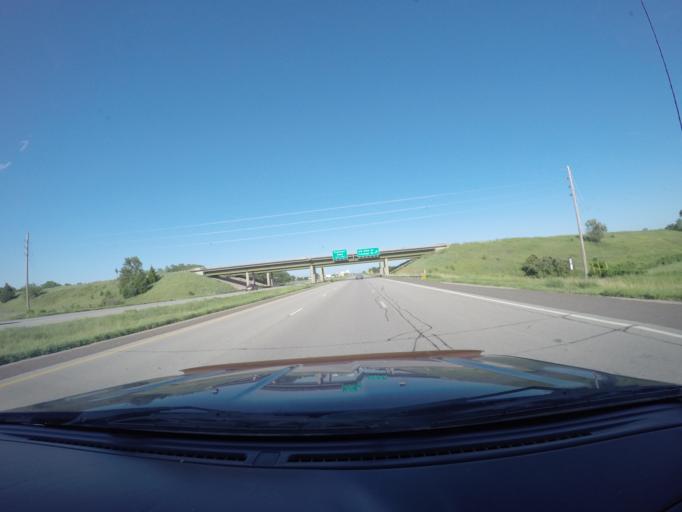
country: US
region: Kansas
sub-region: Shawnee County
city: Topeka
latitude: 39.0906
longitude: -95.7207
